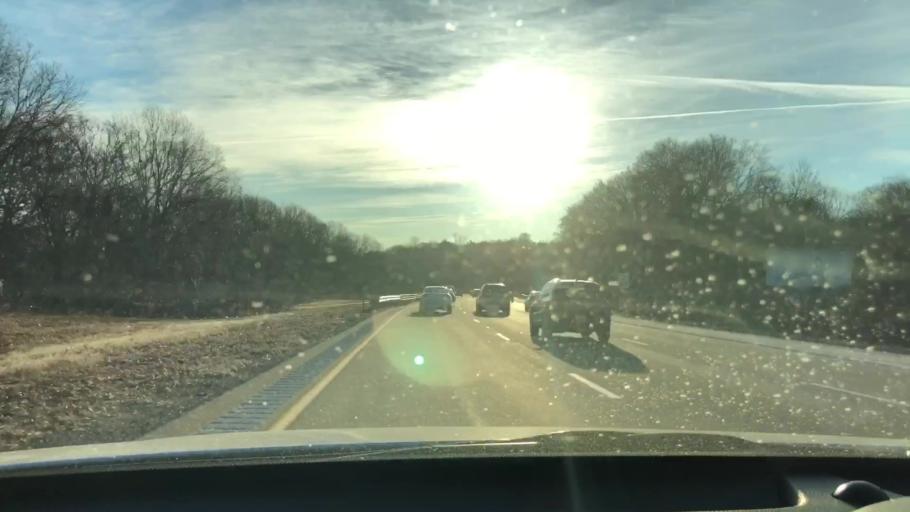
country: US
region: Massachusetts
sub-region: Norfolk County
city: Weymouth
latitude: 42.1922
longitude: -70.9482
